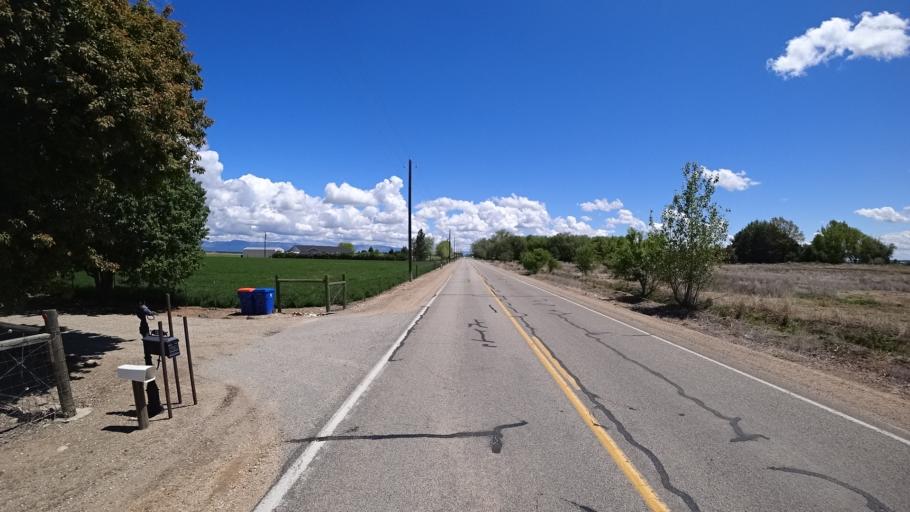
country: US
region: Idaho
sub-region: Ada County
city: Kuna
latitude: 43.5465
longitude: -116.4053
